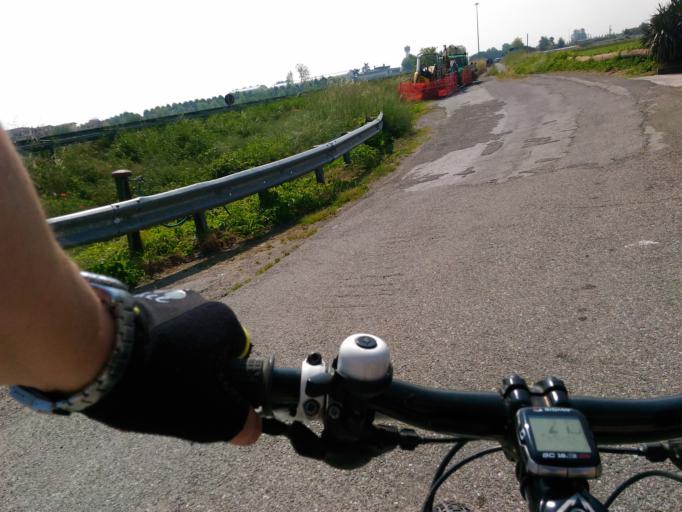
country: IT
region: Lombardy
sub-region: Provincia di Lodi
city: Salerano sul Lambro
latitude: 45.2940
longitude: 9.3737
